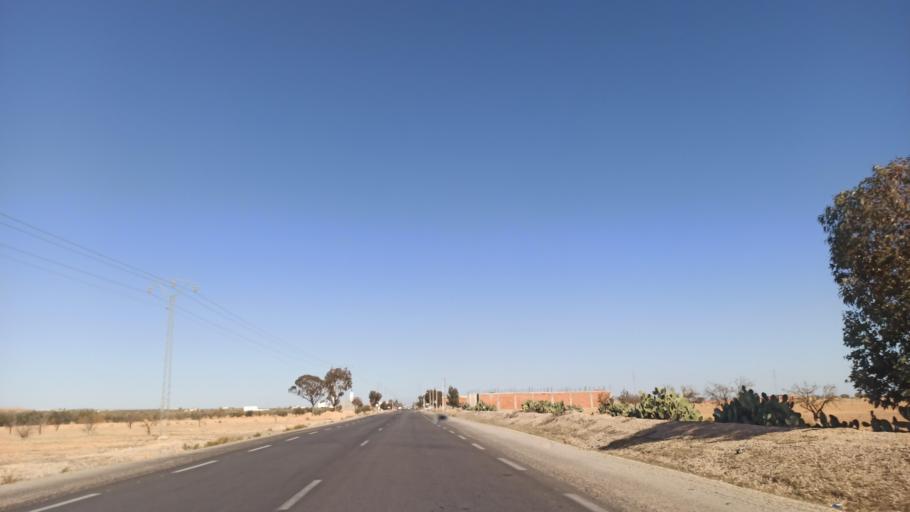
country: TN
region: Sidi Bu Zayd
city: Bi'r al Hufayy
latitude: 34.7381
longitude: 9.0717
